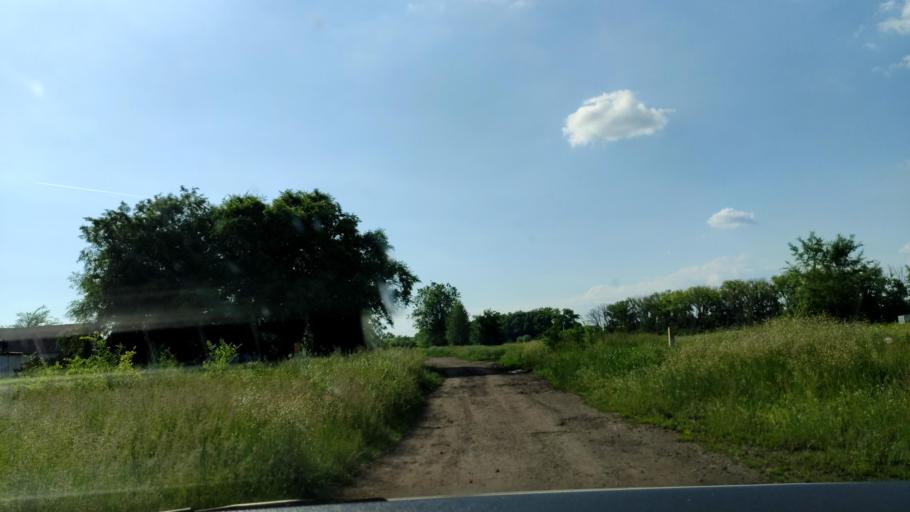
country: RU
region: Voronezj
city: Panino
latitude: 51.6099
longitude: 40.0030
